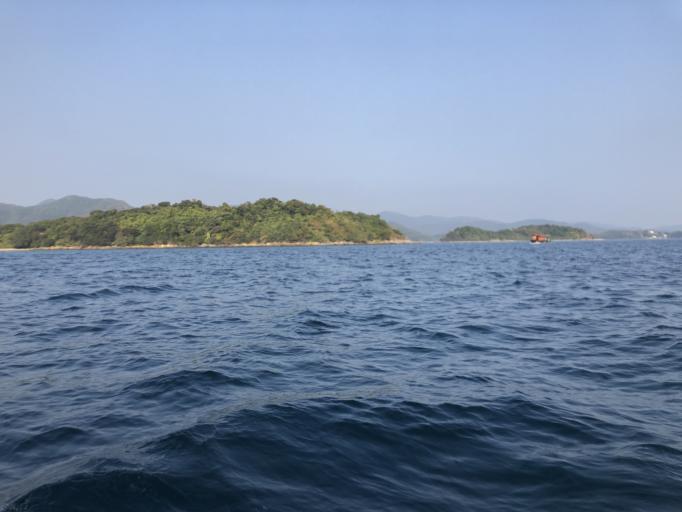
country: HK
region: Sai Kung
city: Sai Kung
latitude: 22.3774
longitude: 114.2788
